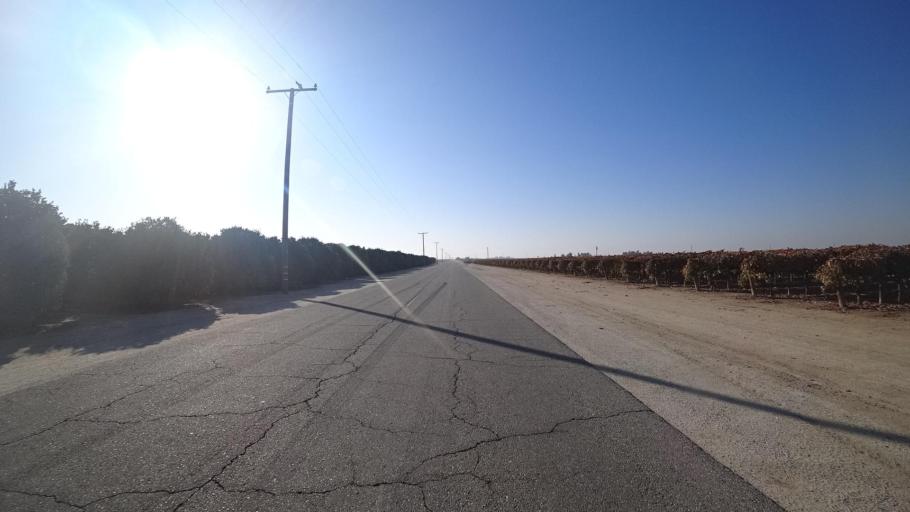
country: US
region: California
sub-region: Tulare County
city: Richgrove
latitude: 35.7852
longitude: -119.1697
